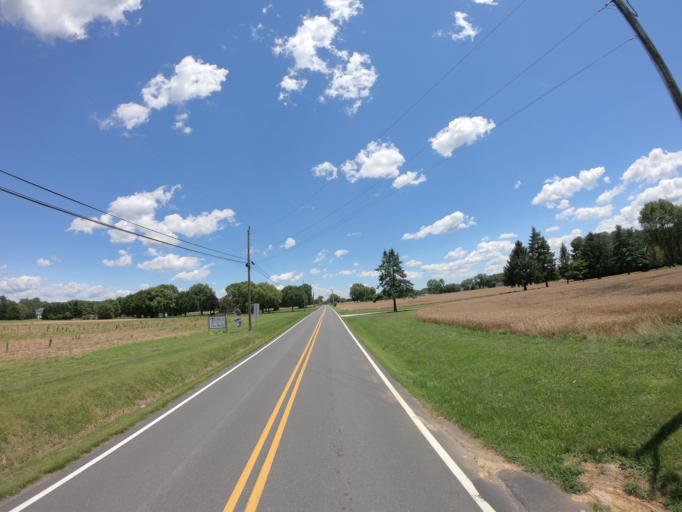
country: US
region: Delaware
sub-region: New Castle County
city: Middletown
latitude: 39.4635
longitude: -75.7615
